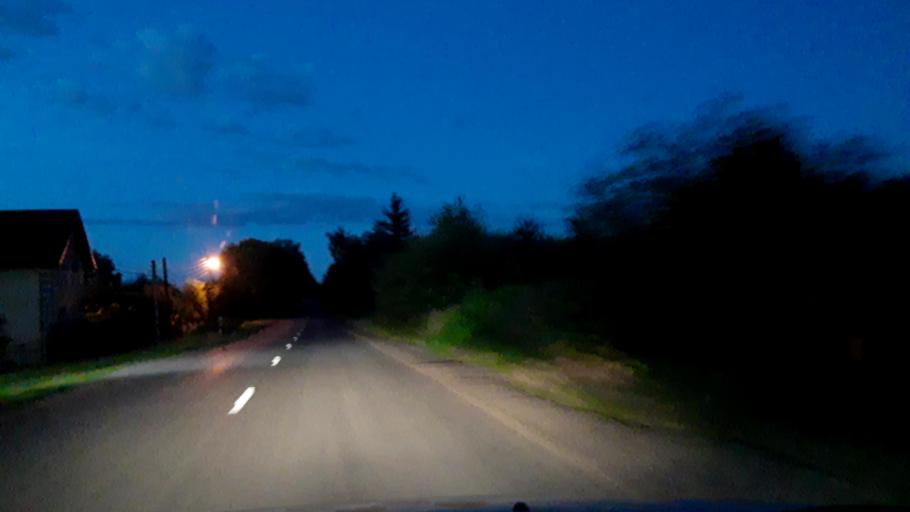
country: RU
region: Nizjnij Novgorod
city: Pamyat' Parizhskoy Kommuny
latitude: 56.0416
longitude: 44.6011
